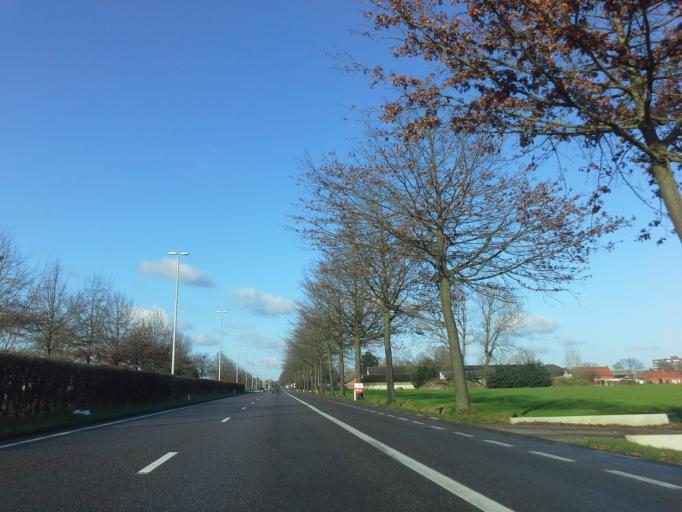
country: BE
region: Flanders
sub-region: Provincie Antwerpen
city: Geel
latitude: 51.1543
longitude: 4.9735
